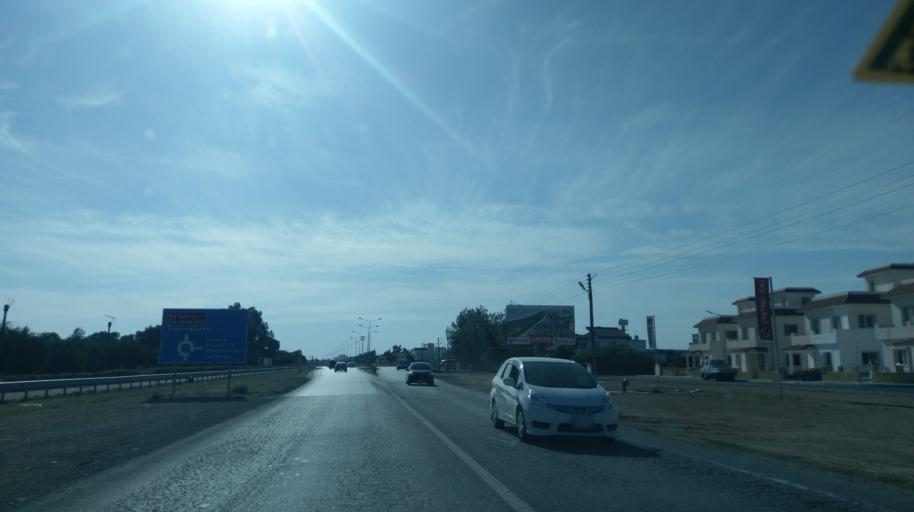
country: CY
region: Ammochostos
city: Trikomo
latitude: 35.2807
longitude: 33.9219
